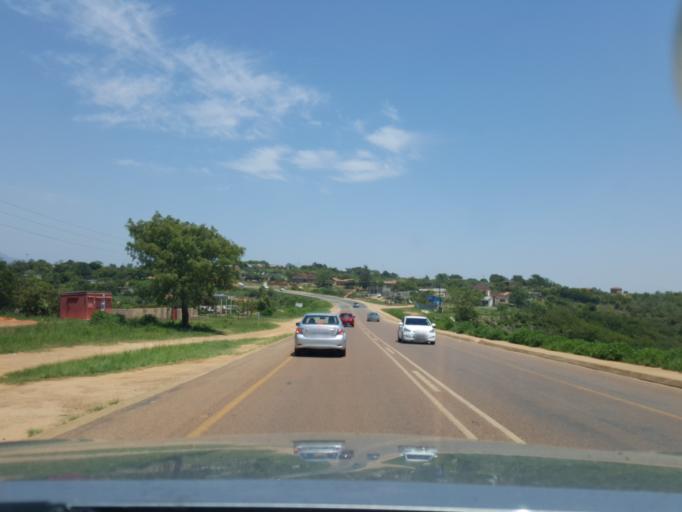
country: ZA
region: Limpopo
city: Thulamahashi
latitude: -24.8461
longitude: 31.0998
